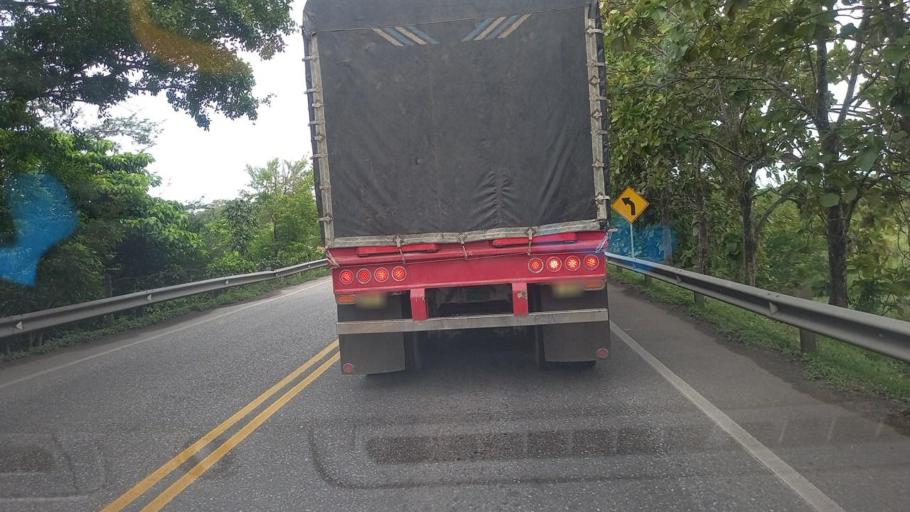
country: CO
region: Antioquia
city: Puerto Triunfo
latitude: 5.8742
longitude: -74.5674
